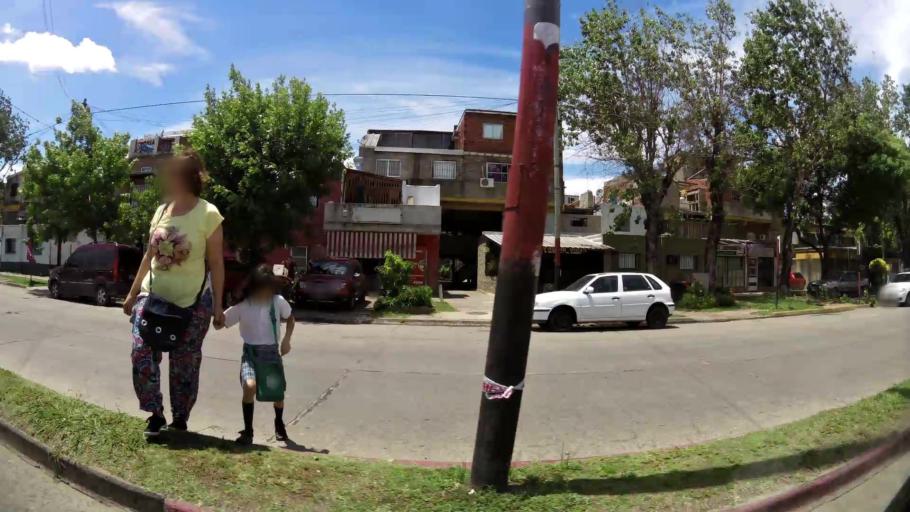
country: AR
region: Santa Fe
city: Gobernador Galvez
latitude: -32.9949
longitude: -60.6287
